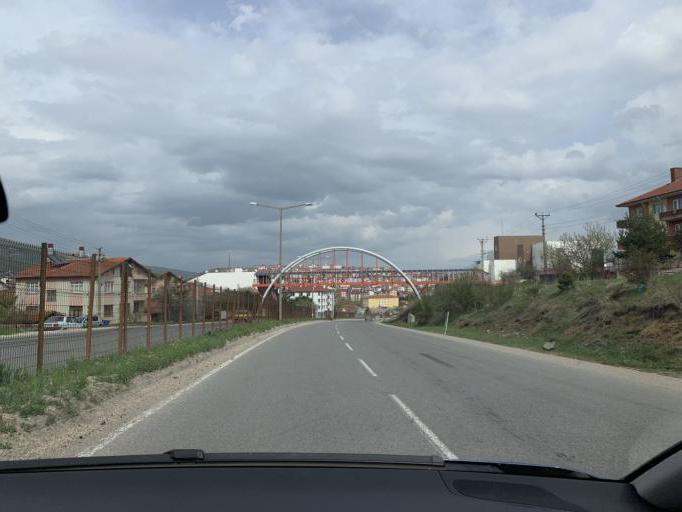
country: TR
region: Bolu
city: Gerede
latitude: 40.7964
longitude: 32.1974
